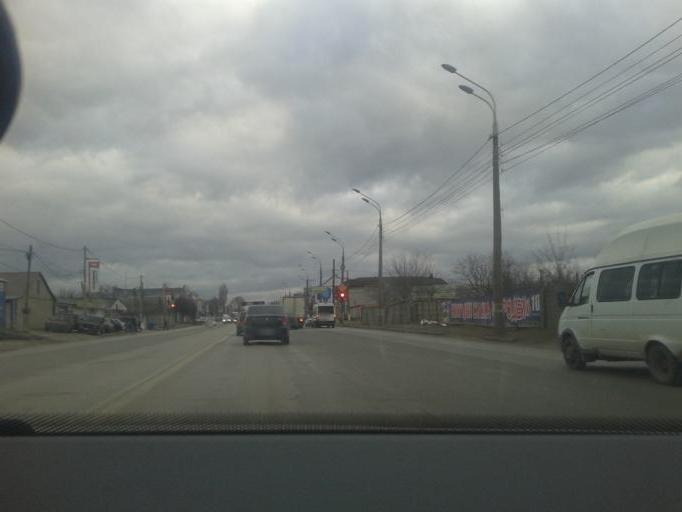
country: RU
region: Volgograd
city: Volgograd
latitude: 48.6925
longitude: 44.4626
